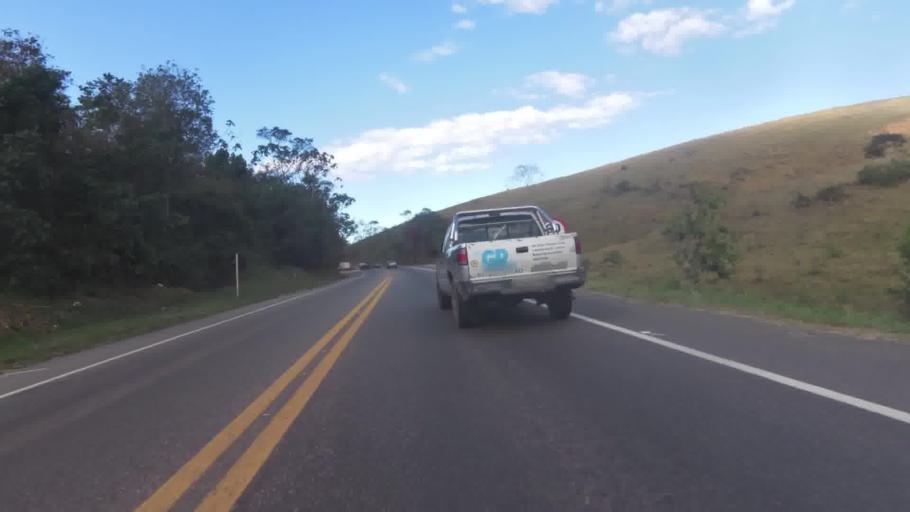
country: BR
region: Espirito Santo
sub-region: Rio Novo Do Sul
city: Rio Novo do Sul
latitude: -20.8665
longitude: -40.8902
